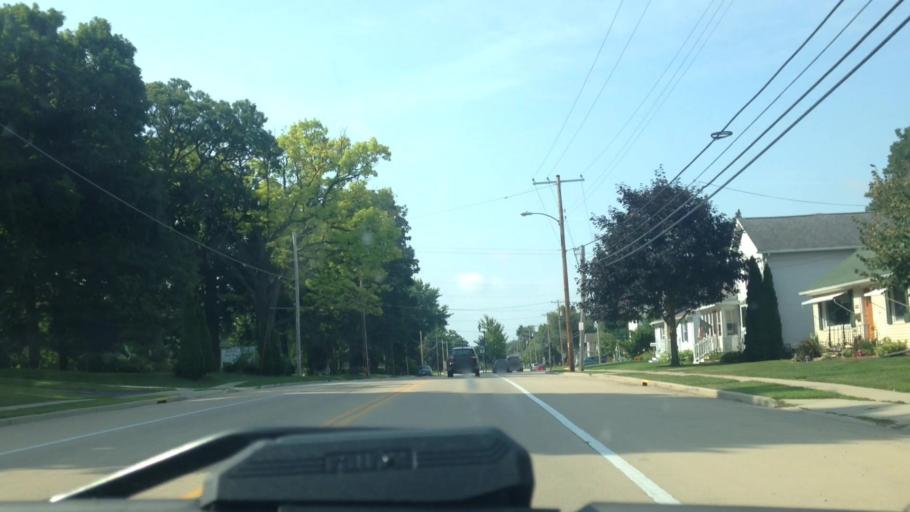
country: US
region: Wisconsin
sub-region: Dodge County
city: Mayville
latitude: 43.5043
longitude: -88.5430
